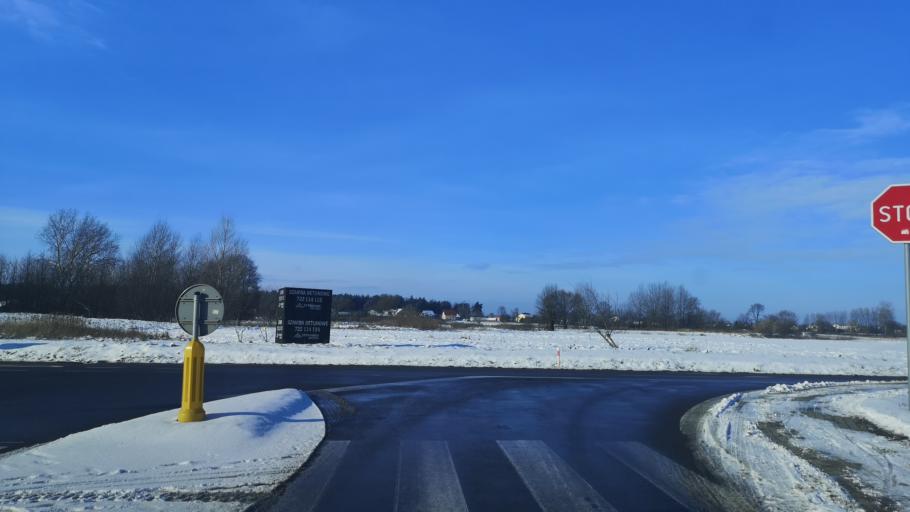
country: PL
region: Subcarpathian Voivodeship
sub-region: Powiat przeworski
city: Gorliczyna
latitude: 50.0964
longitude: 22.4922
